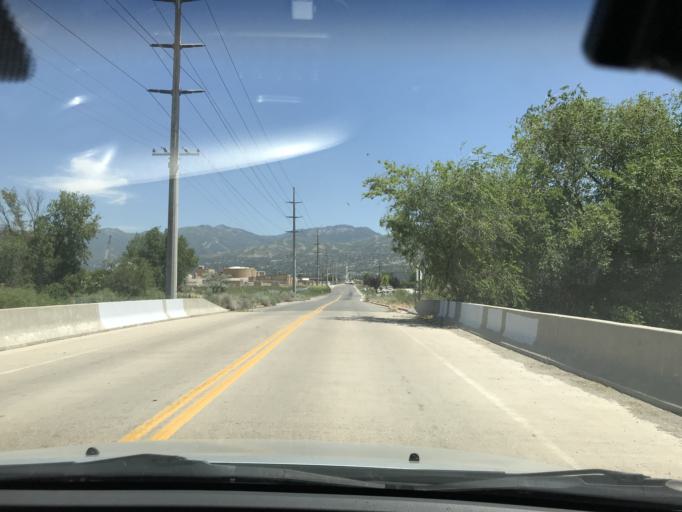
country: US
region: Utah
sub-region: Davis County
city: North Salt Lake
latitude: 40.8420
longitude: -111.9513
